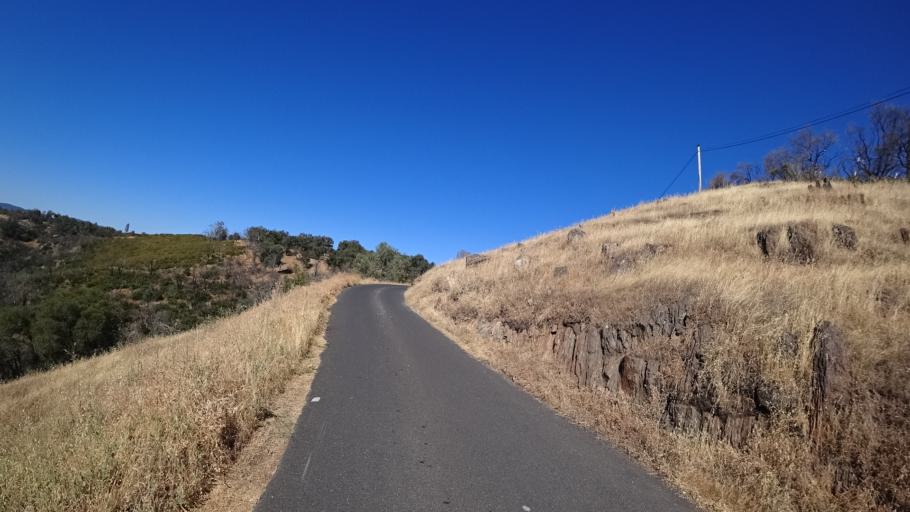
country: US
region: California
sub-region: Calaveras County
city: San Andreas
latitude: 38.2312
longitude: -120.6588
